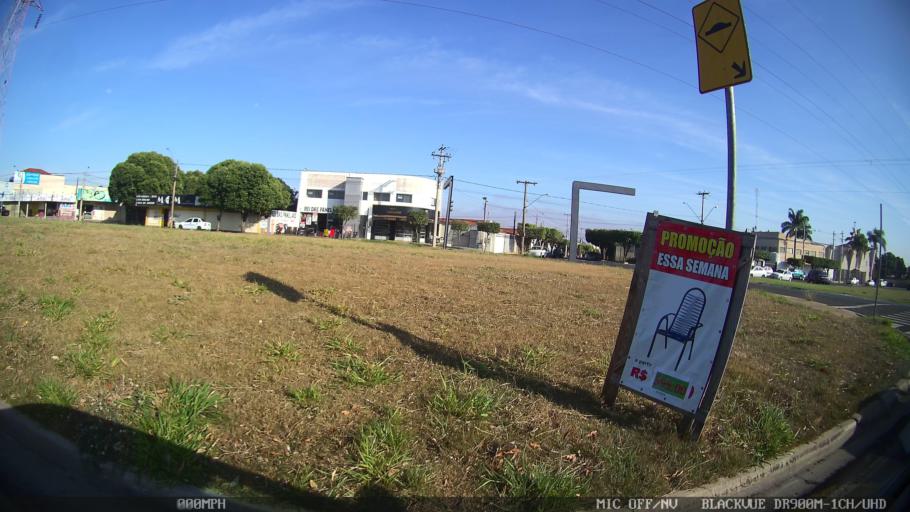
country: BR
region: Sao Paulo
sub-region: Sao Jose Do Rio Preto
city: Sao Jose do Rio Preto
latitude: -20.7922
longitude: -49.3443
